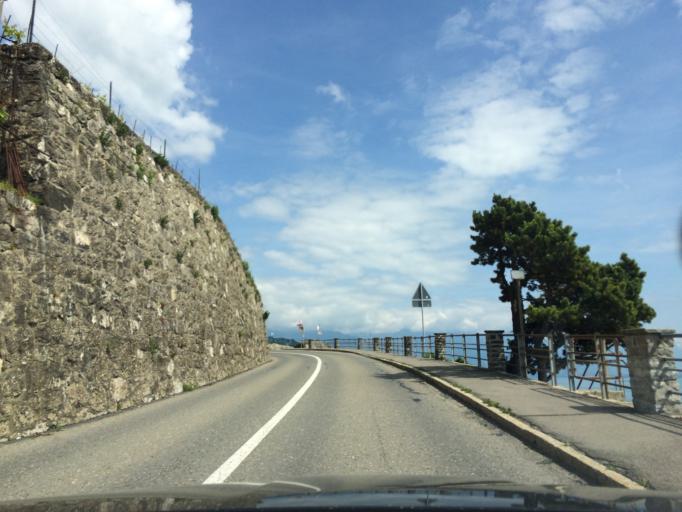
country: CH
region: Vaud
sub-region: Lavaux-Oron District
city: Chexbres
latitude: 46.4805
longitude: 6.7665
